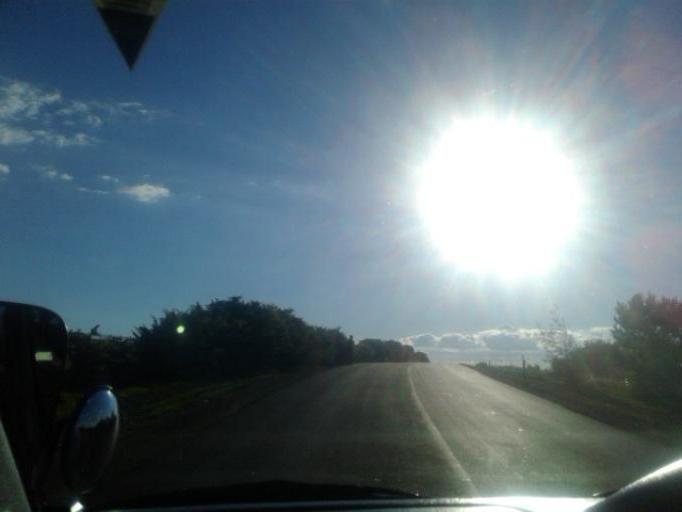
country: LS
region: Maseru
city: Maseru
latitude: -29.3165
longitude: 27.5892
